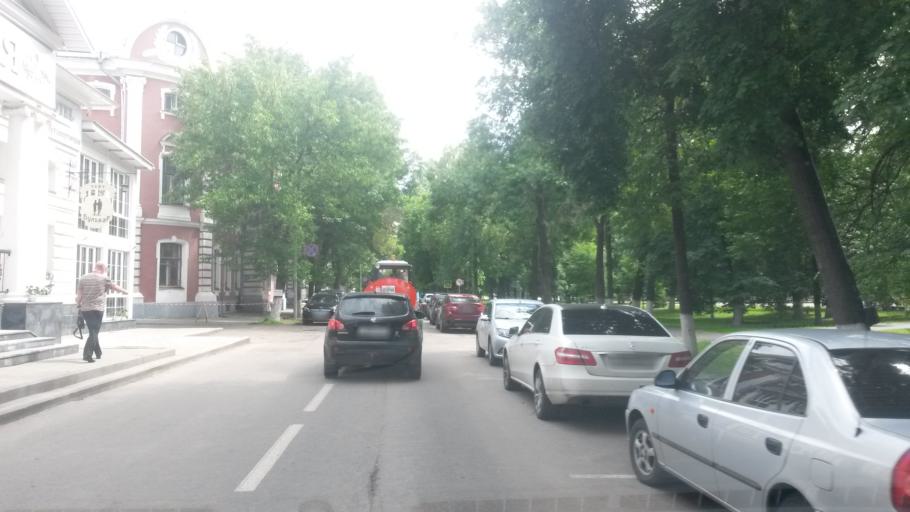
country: RU
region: Jaroslavl
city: Yaroslavl
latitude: 57.6259
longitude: 39.8969
